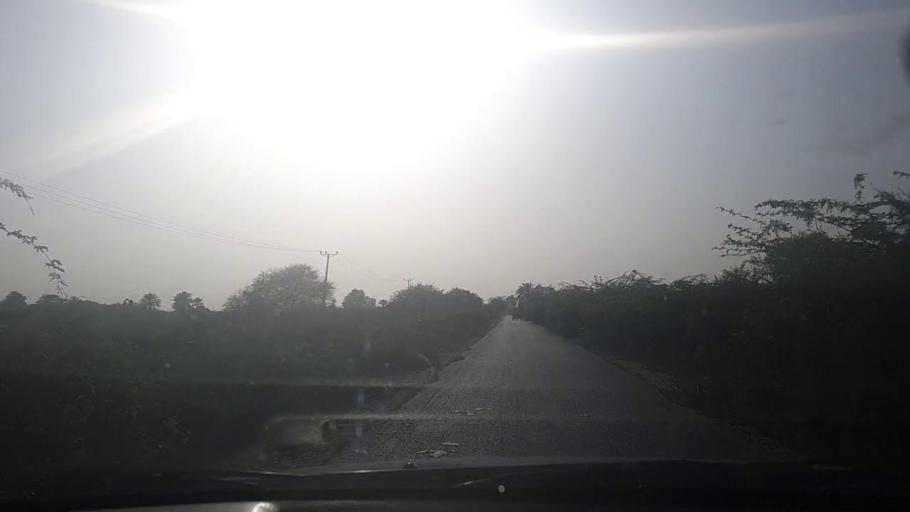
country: PK
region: Sindh
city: Keti Bandar
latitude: 24.2914
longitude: 67.6136
